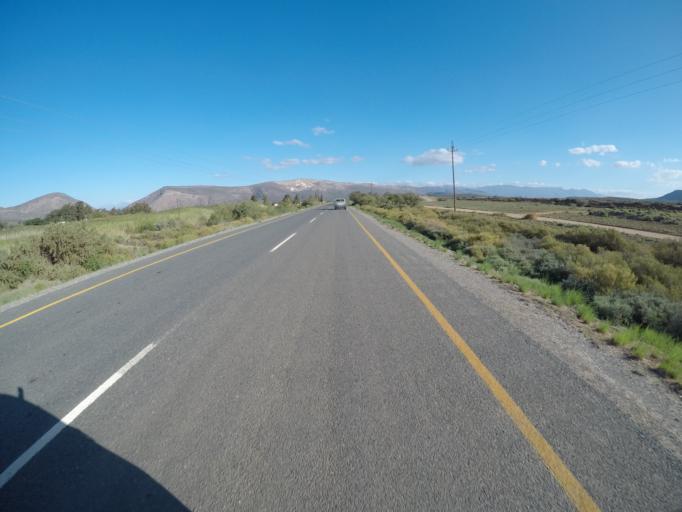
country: ZA
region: Western Cape
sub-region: Cape Winelands District Municipality
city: Ashton
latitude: -33.8039
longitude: 19.7819
